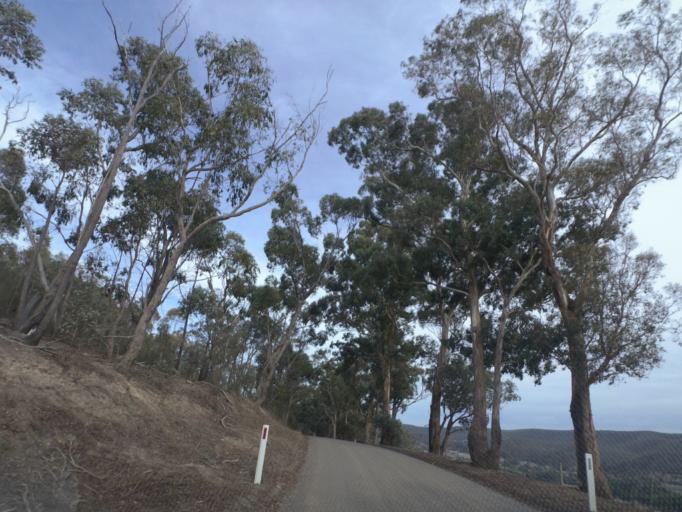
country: AU
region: Victoria
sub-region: Yarra Ranges
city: Yarra Glen
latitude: -37.5944
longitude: 145.3897
